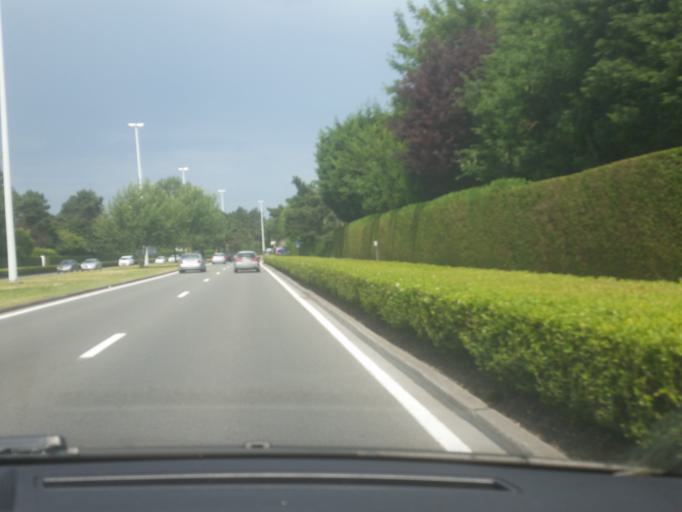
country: BE
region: Flanders
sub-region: Provincie West-Vlaanderen
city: Ostend
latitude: 51.2179
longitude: 2.9225
